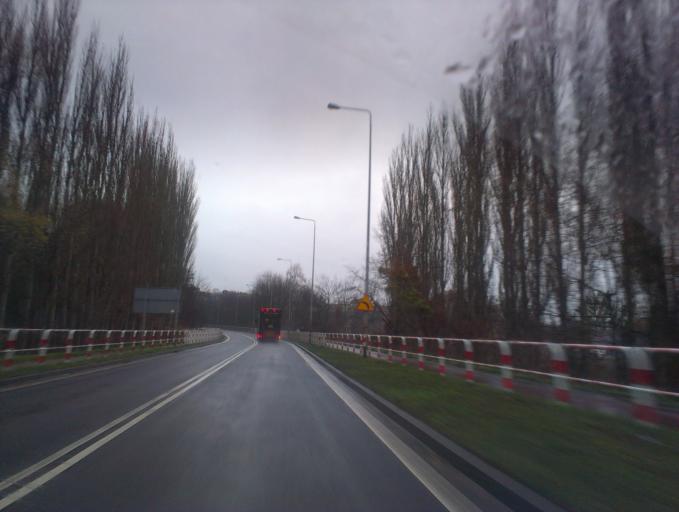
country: PL
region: Greater Poland Voivodeship
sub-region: Powiat chodzieski
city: Chodziez
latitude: 52.9858
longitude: 16.9203
